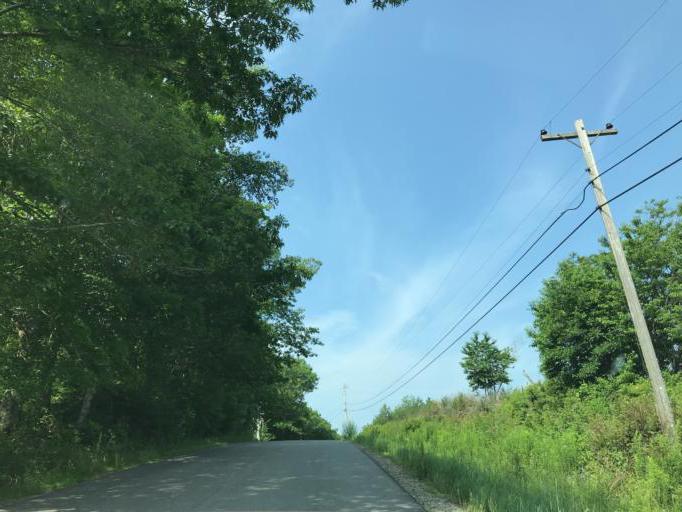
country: US
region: Maine
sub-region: Knox County
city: Hope
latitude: 44.2304
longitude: -69.1535
